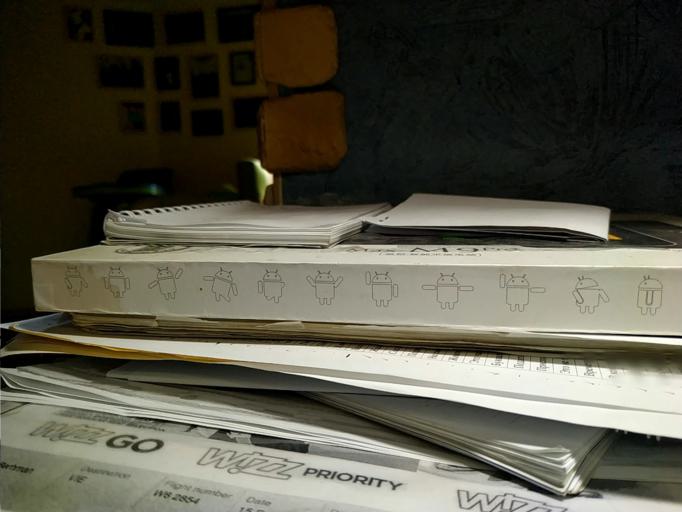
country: RU
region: Novgorod
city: Poddor'ye
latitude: 57.5254
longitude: 30.9107
